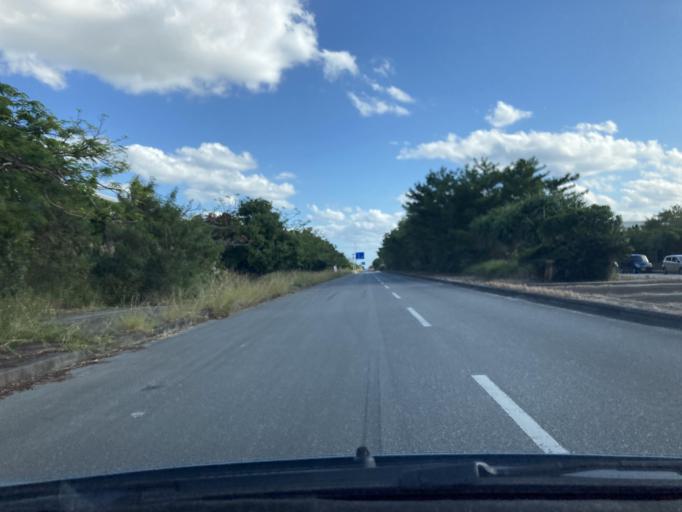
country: JP
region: Okinawa
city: Katsuren-haebaru
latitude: 26.3393
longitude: 127.8602
